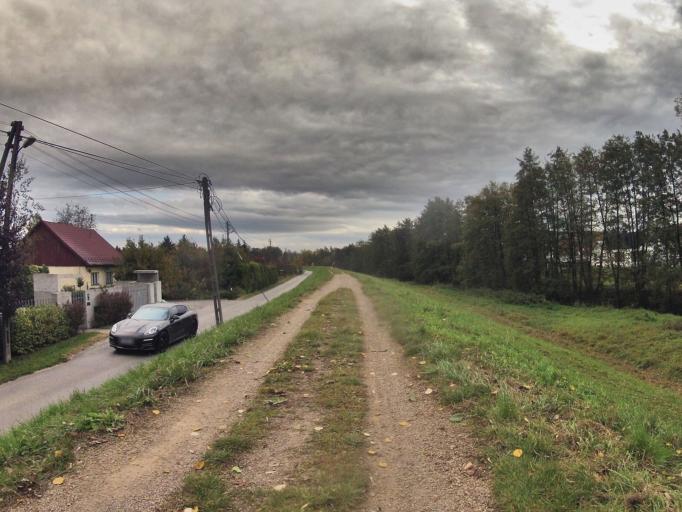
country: PL
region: Lesser Poland Voivodeship
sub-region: Powiat krakowski
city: Rzaska
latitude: 50.0698
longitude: 19.8791
